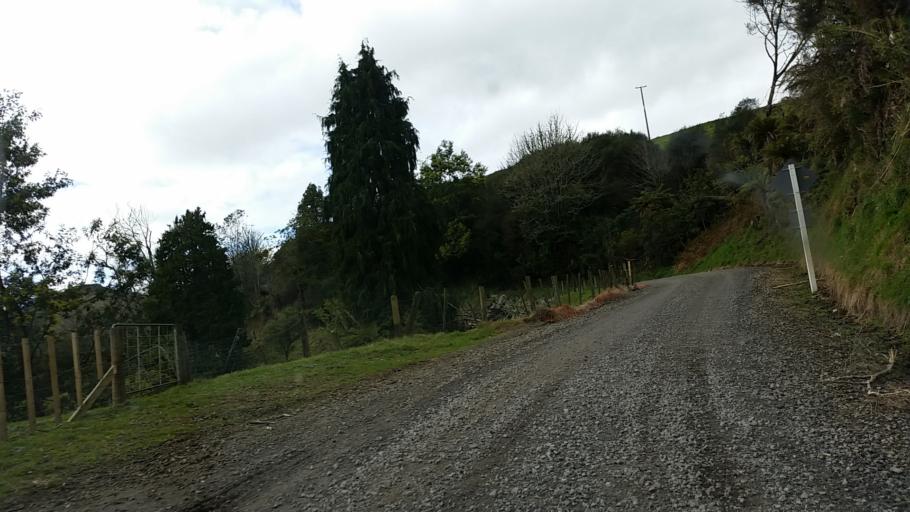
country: NZ
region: Taranaki
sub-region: New Plymouth District
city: Waitara
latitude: -39.1640
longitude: 174.5725
